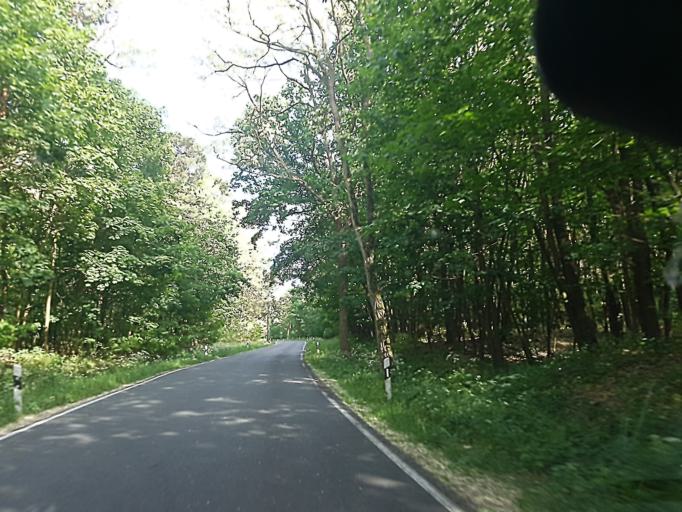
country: DE
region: Saxony-Anhalt
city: Kropstadt
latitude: 51.9854
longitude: 12.6977
